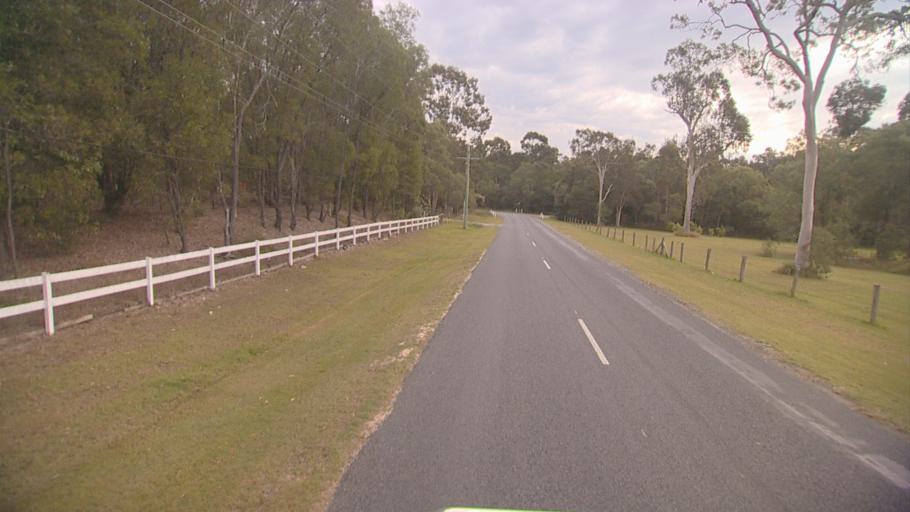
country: AU
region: Queensland
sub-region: Logan
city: Chambers Flat
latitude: -27.7835
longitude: 153.1114
